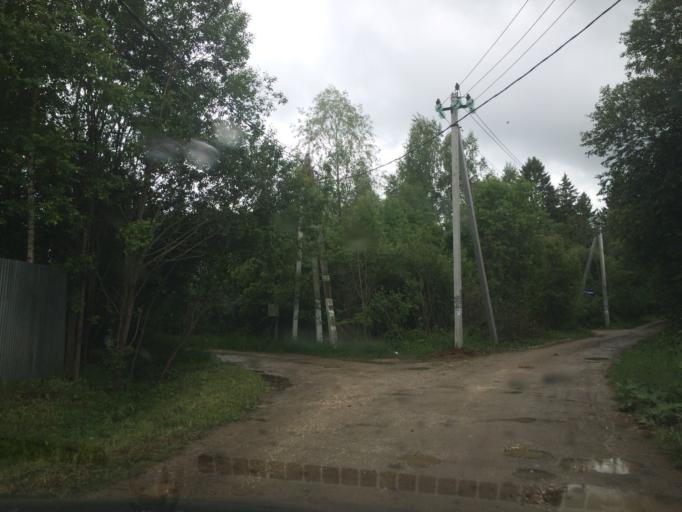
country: RU
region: Moskovskaya
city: Solnechnogorsk
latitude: 56.1604
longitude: 37.0073
